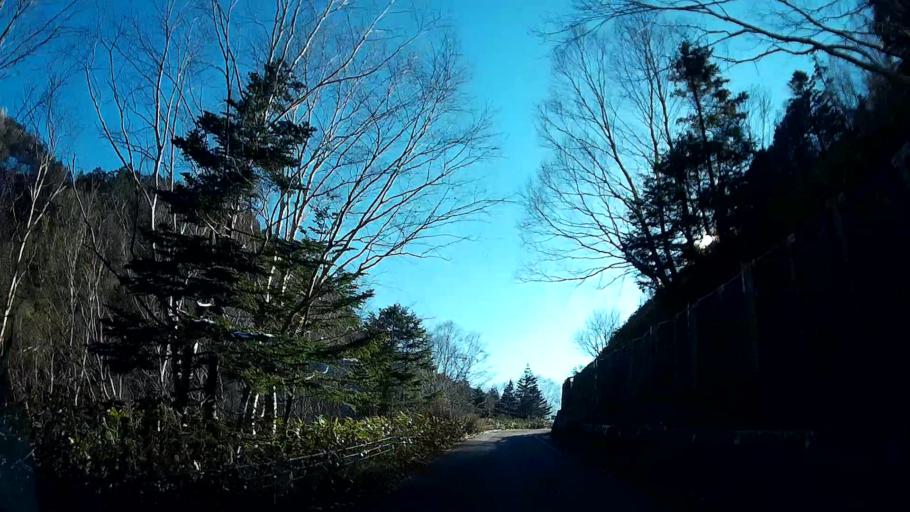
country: JP
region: Nagano
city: Hotaka
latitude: 36.1958
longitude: 137.5851
